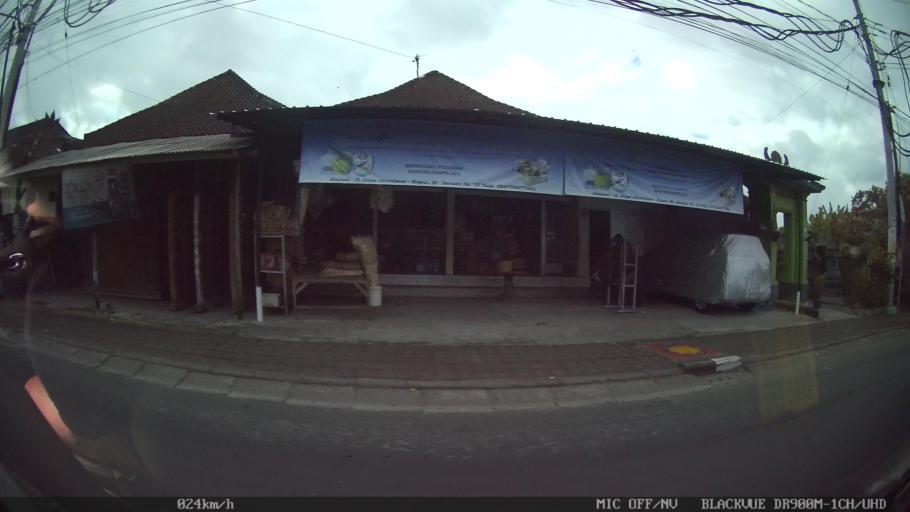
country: ID
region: Bali
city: Banjar Pekenjelodan
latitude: -8.5878
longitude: 115.1790
